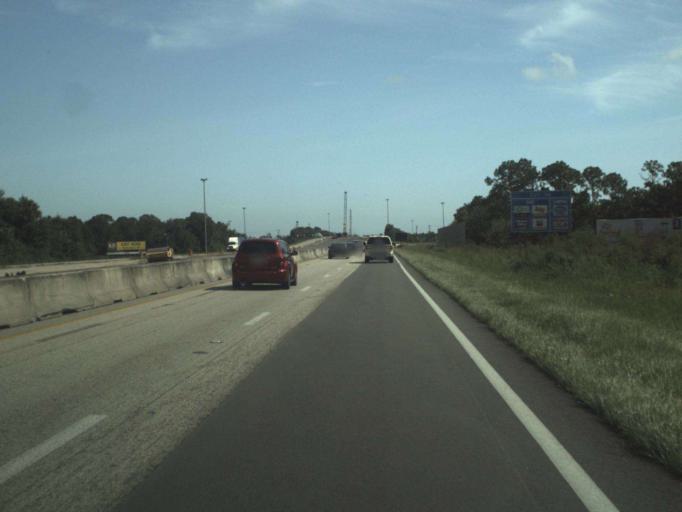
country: US
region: Florida
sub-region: Indian River County
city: Fellsmere
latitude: 27.7605
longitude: -80.5513
